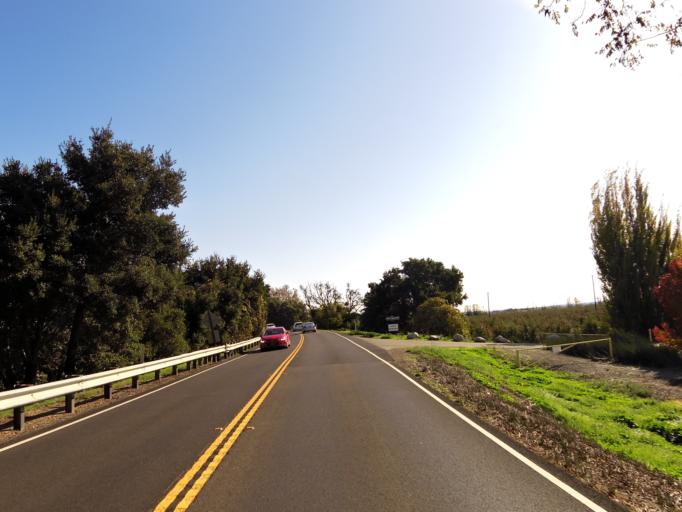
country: US
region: California
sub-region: Solano County
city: Rio Vista
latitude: 38.1661
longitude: -121.6284
